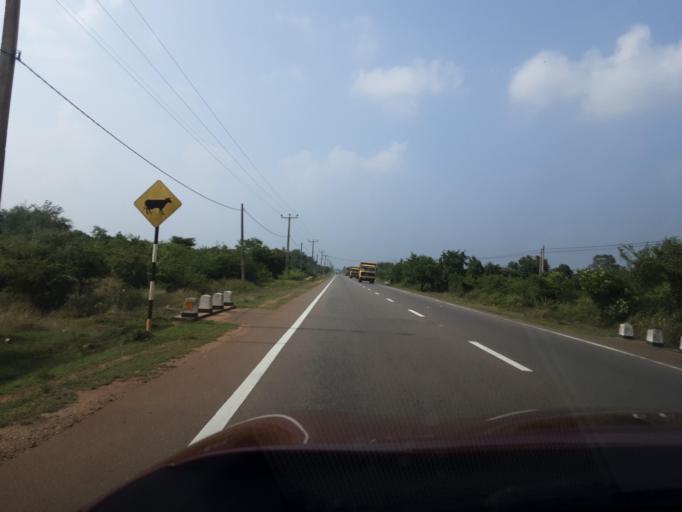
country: LK
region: Northern Province
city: Kilinochchi
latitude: 9.0805
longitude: 80.4826
